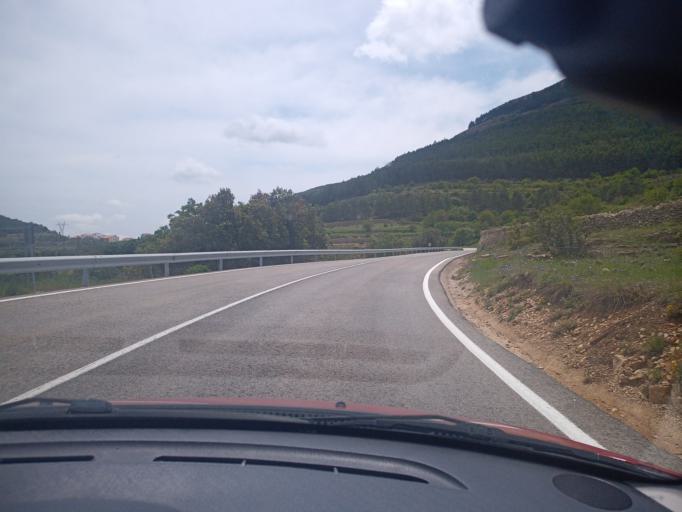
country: ES
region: Valencia
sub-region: Provincia de Castello
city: Ares del Maestre
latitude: 40.4595
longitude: -0.1492
